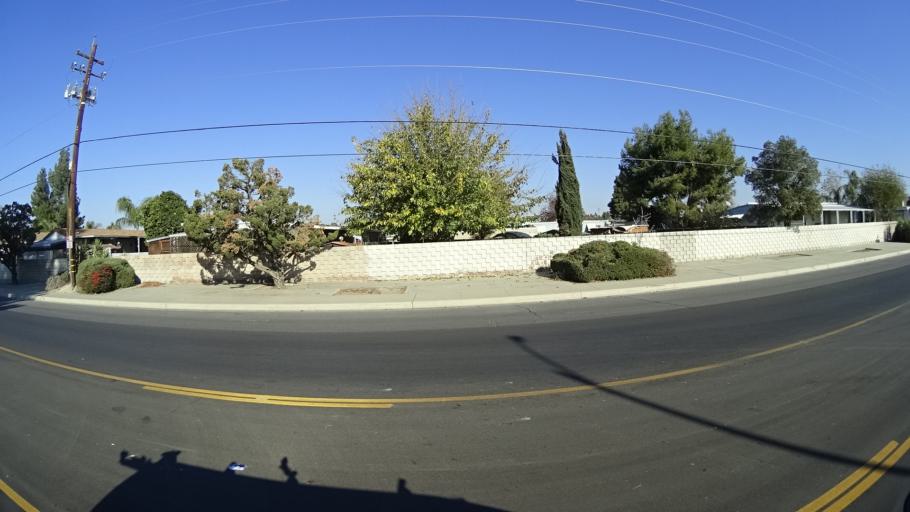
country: US
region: California
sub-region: Kern County
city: Greenfield
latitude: 35.3103
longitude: -119.0199
